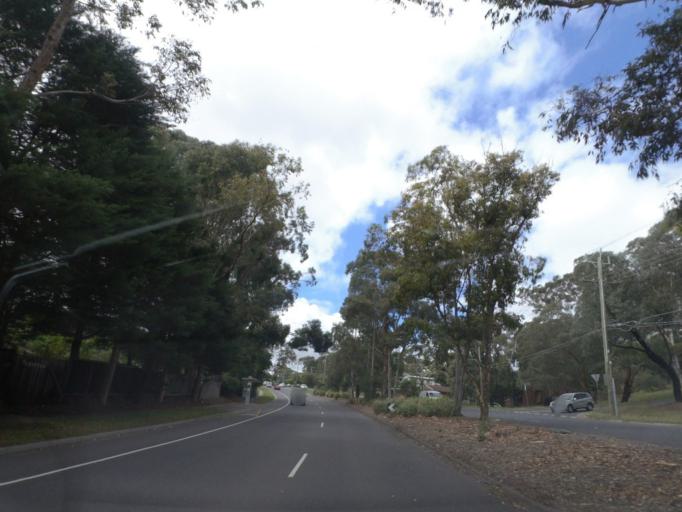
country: AU
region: Victoria
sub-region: Banyule
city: Greensborough
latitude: -37.6938
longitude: 145.1122
